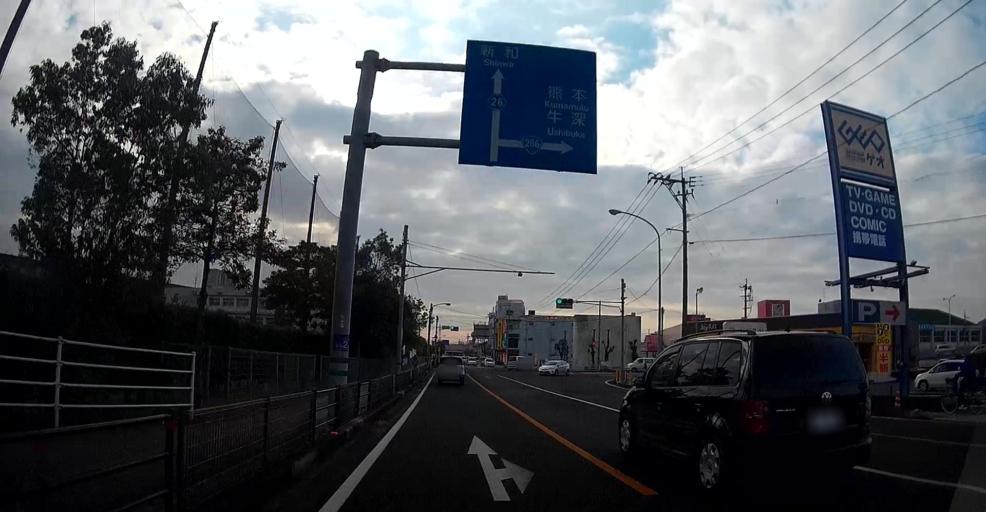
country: JP
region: Kumamoto
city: Hondo
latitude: 32.4470
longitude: 130.2010
